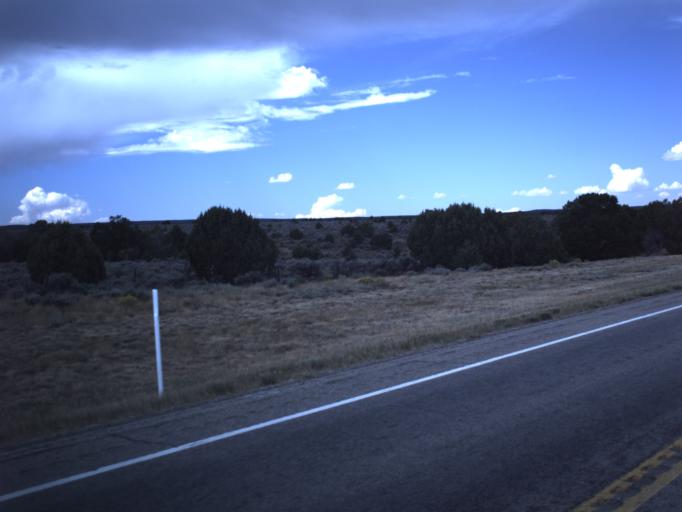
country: US
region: Utah
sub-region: San Juan County
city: Monticello
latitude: 37.9071
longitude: -109.3457
